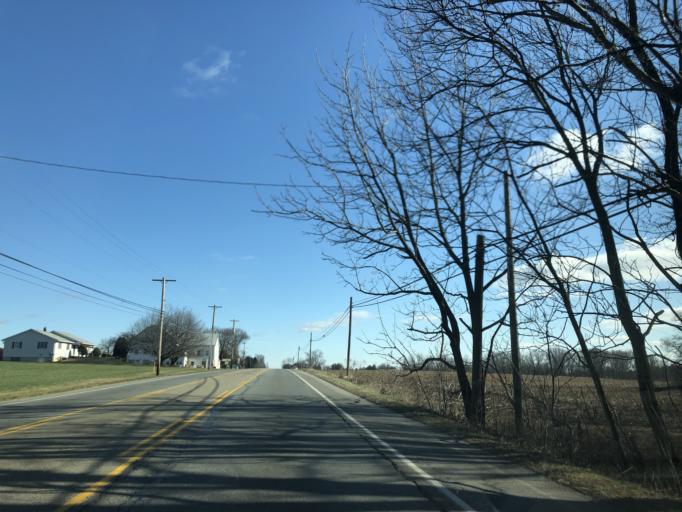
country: US
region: Pennsylvania
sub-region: Chester County
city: Atglen
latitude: 39.9864
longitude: -75.9605
